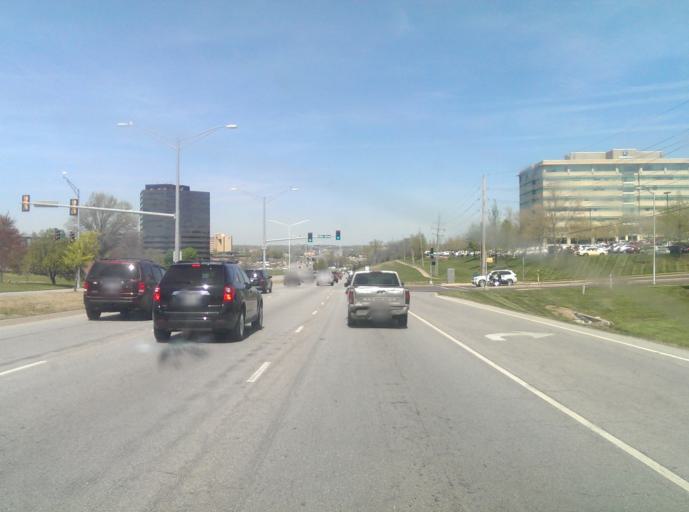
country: US
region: Kansas
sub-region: Johnson County
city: Overland Park
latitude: 38.9215
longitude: -94.6673
